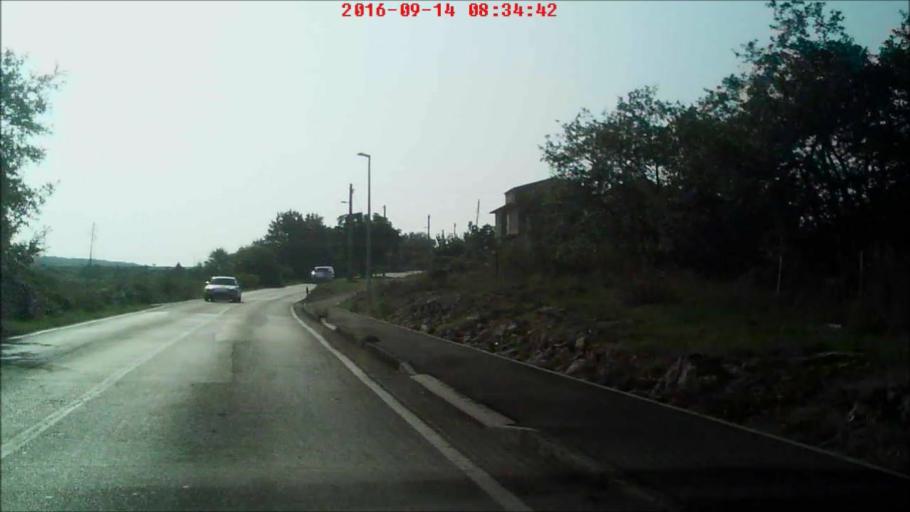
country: HR
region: Zadarska
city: Policnik
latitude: 44.1505
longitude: 15.3239
